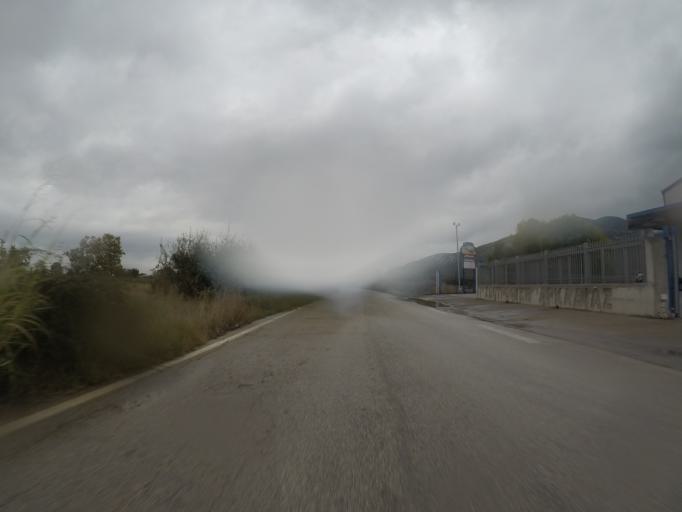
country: GR
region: Peloponnese
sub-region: Nomos Arkadias
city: Tripoli
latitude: 37.5764
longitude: 22.4138
